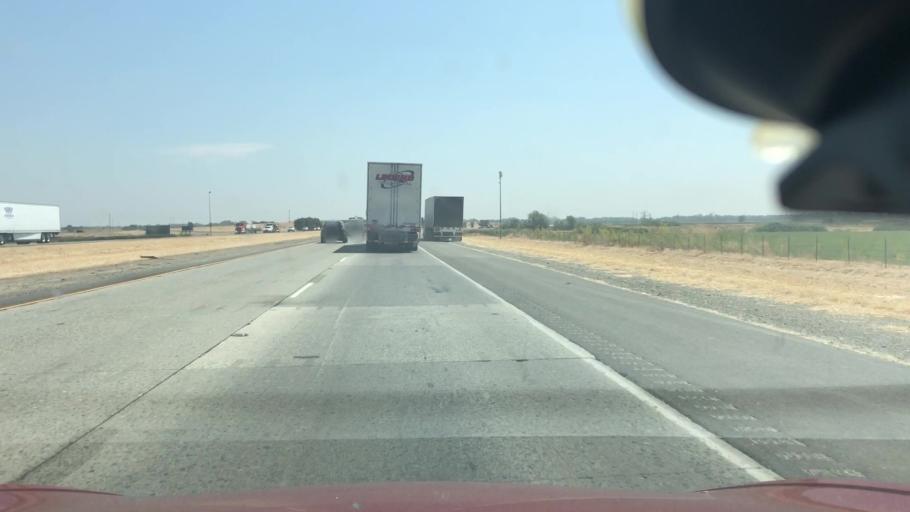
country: US
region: California
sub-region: Sacramento County
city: Walnut Grove
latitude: 38.2912
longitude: -121.4596
